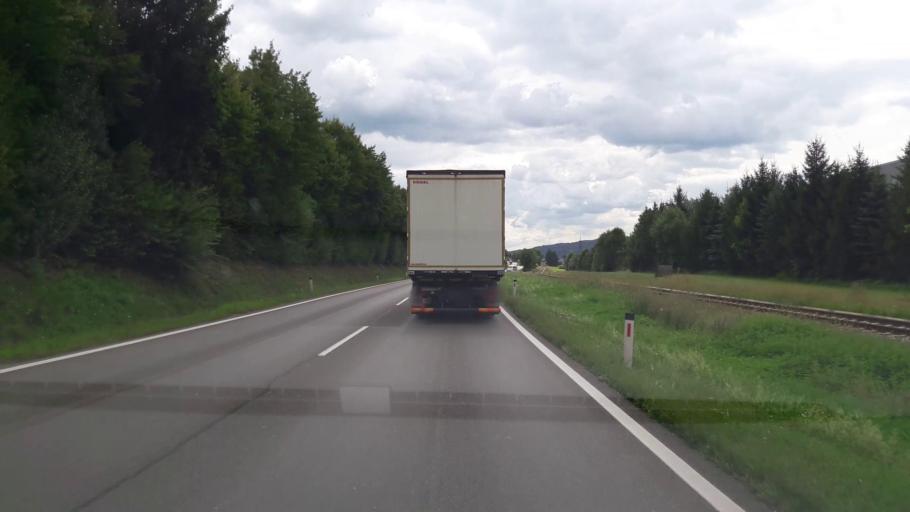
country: AT
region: Styria
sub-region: Politischer Bezirk Weiz
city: Gleisdorf
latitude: 47.1195
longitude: 15.6992
